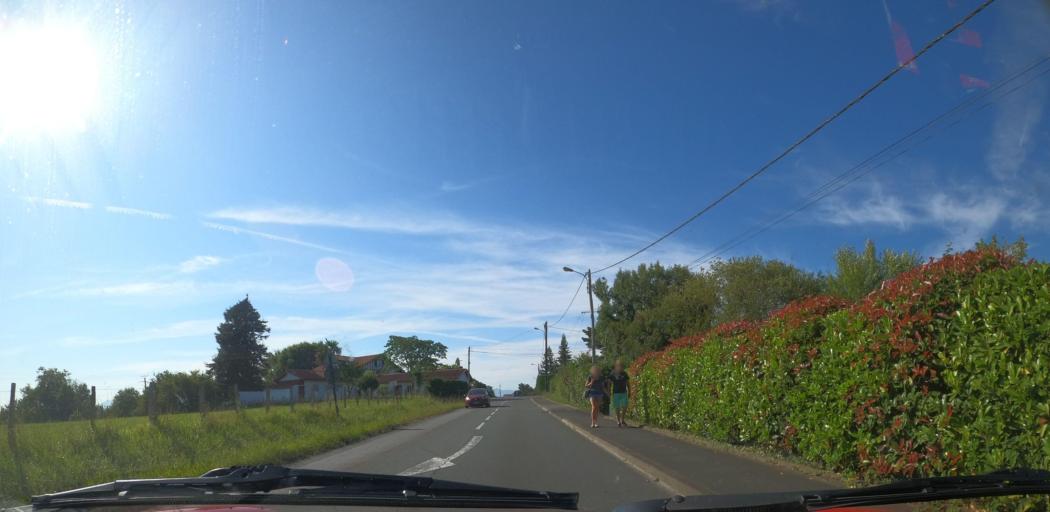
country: FR
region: Aquitaine
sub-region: Departement des Pyrenees-Atlantiques
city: Arbonne
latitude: 43.4276
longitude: -1.5489
